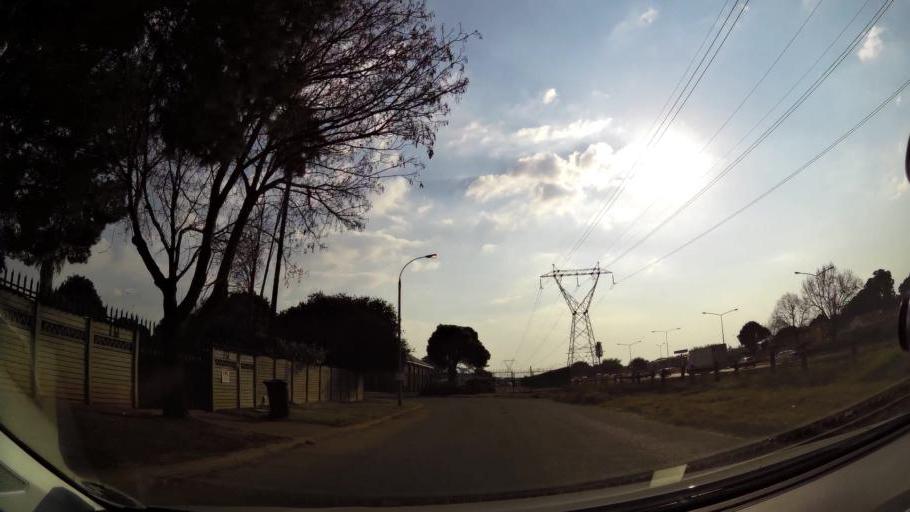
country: ZA
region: Gauteng
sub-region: City of Johannesburg Metropolitan Municipality
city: Modderfontein
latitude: -26.0955
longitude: 28.1990
